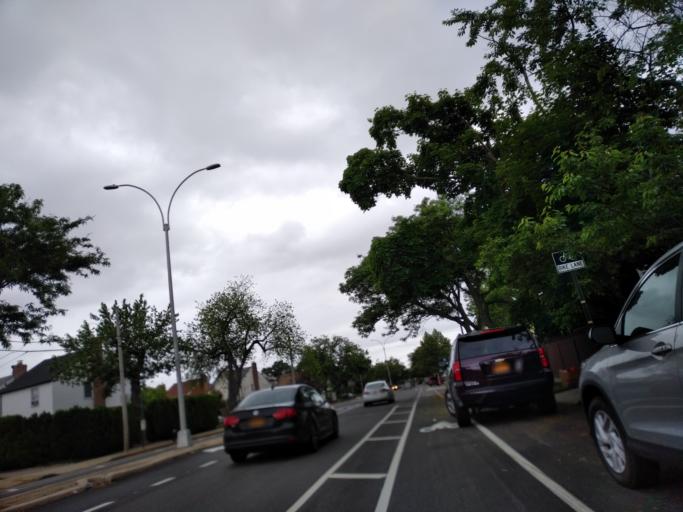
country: US
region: New York
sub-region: Nassau County
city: East Atlantic Beach
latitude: 40.7750
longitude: -73.7929
